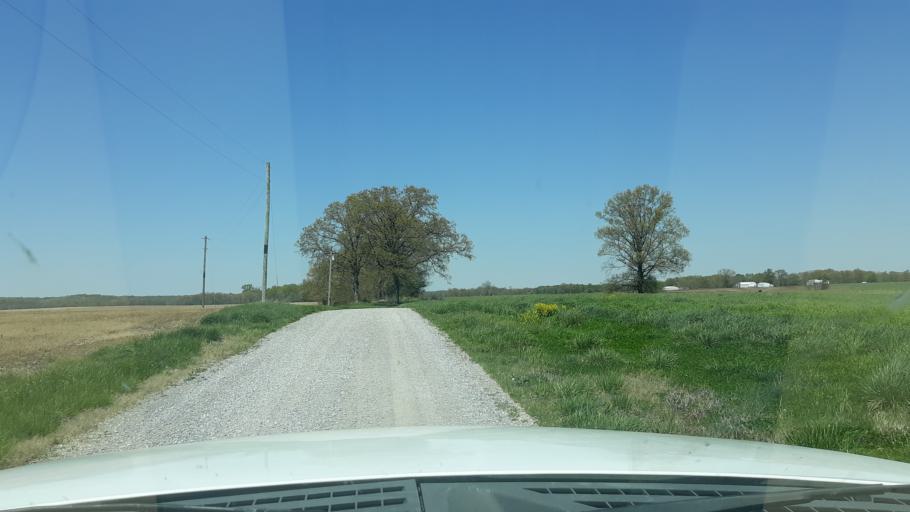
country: US
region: Illinois
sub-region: Saline County
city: Harrisburg
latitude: 37.8840
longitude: -88.6421
